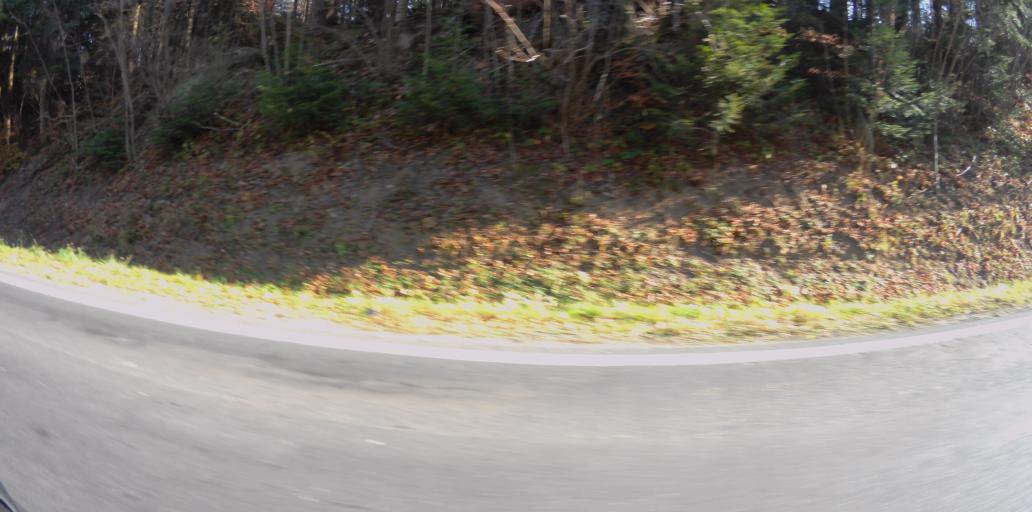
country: PL
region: Subcarpathian Voivodeship
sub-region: Powiat bieszczadzki
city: Ustrzyki Dolne
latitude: 49.5218
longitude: 22.6033
